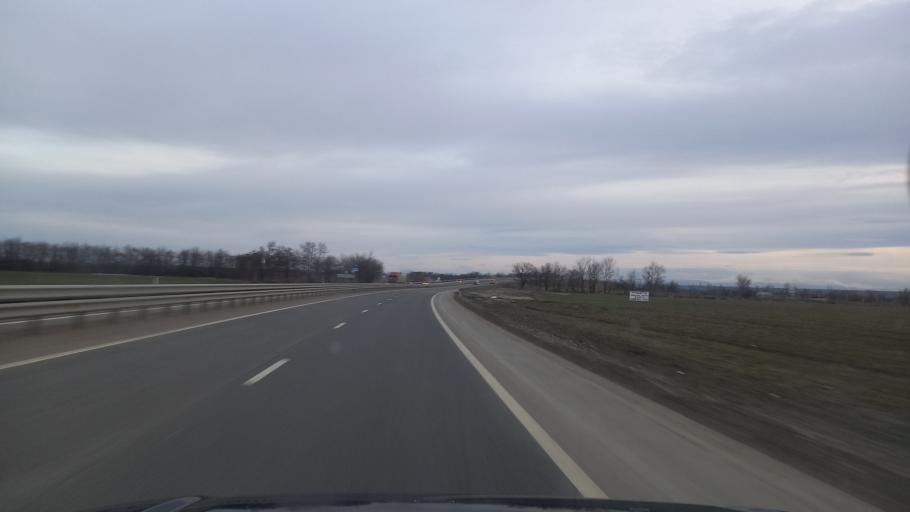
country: RU
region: Adygeya
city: Khanskaya
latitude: 44.7071
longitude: 39.9673
